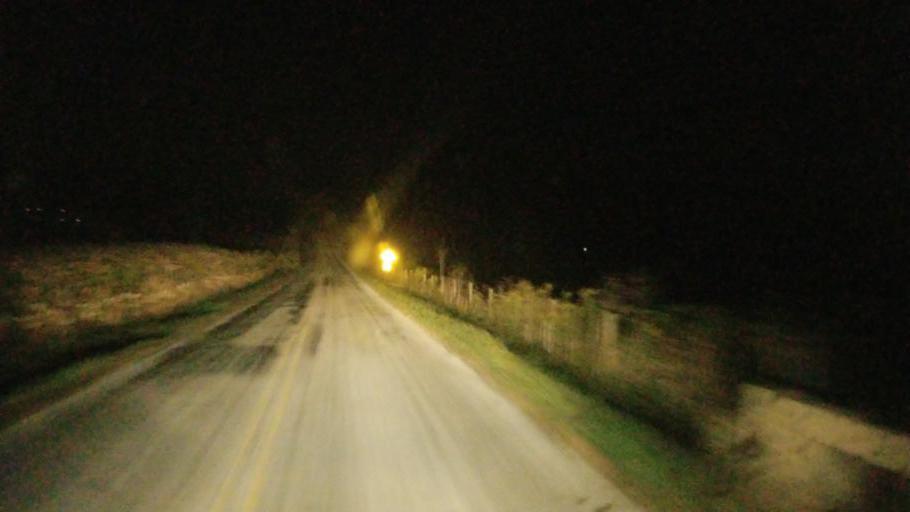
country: US
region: Ohio
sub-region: Ashland County
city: Loudonville
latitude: 40.5782
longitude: -82.3606
